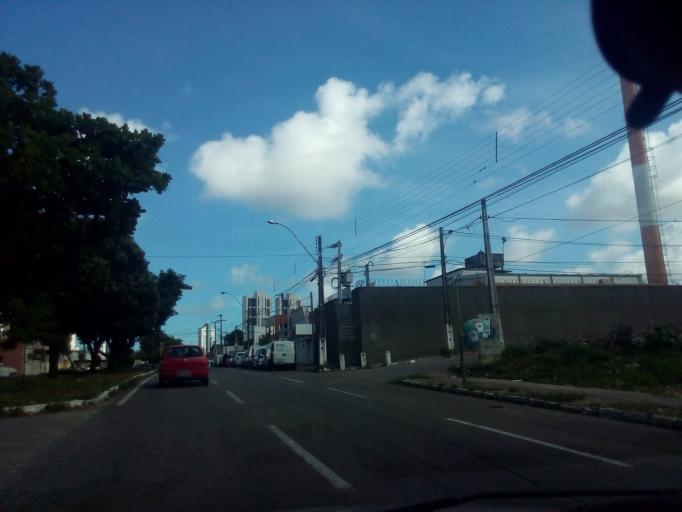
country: BR
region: Rio Grande do Norte
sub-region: Natal
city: Natal
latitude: -5.8020
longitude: -35.2111
